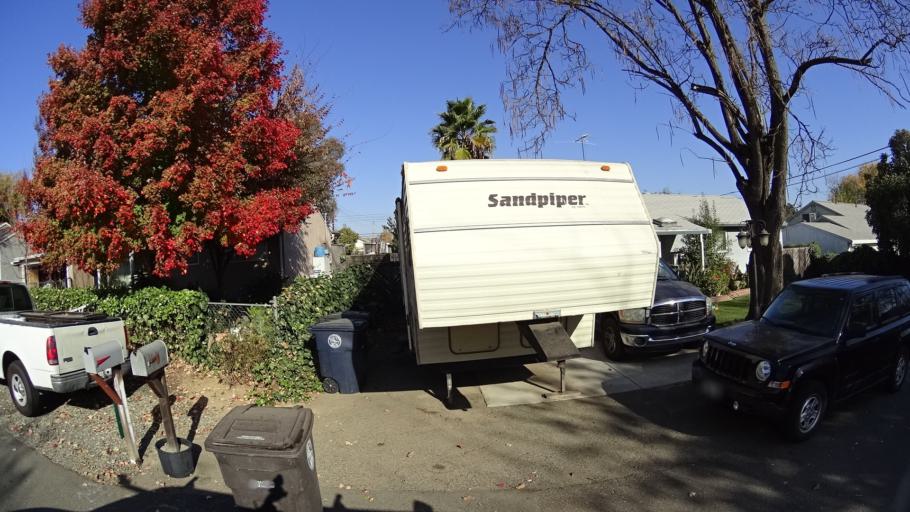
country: US
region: California
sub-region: Sacramento County
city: Citrus Heights
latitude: 38.6933
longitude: -121.2841
